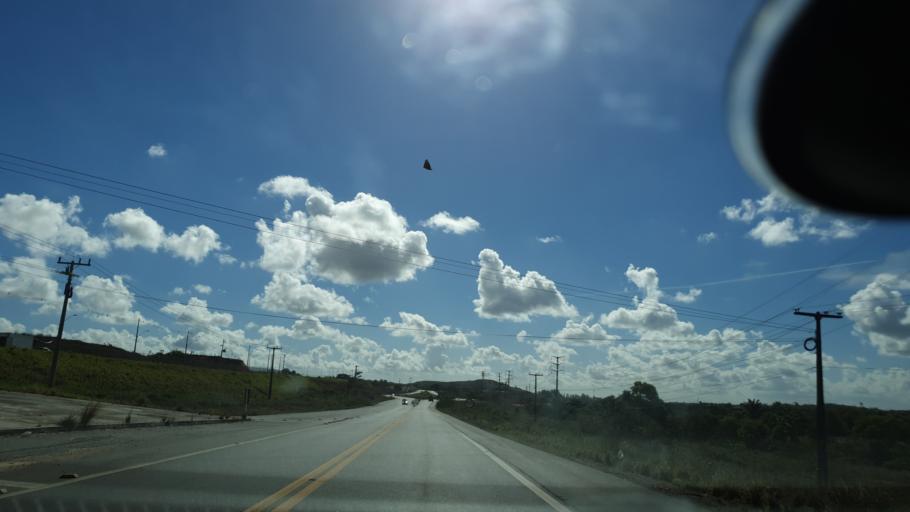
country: BR
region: Bahia
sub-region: Camacari
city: Camacari
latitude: -12.6818
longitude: -38.2436
